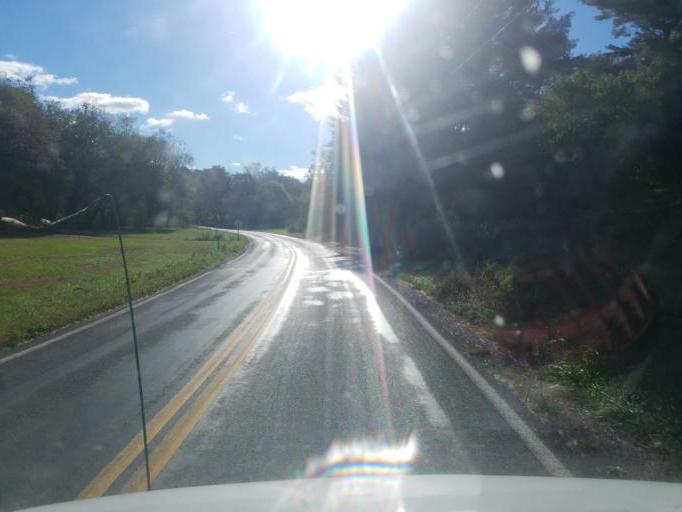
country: US
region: Pennsylvania
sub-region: Franklin County
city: Waynesboro
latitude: 39.8032
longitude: -77.6107
